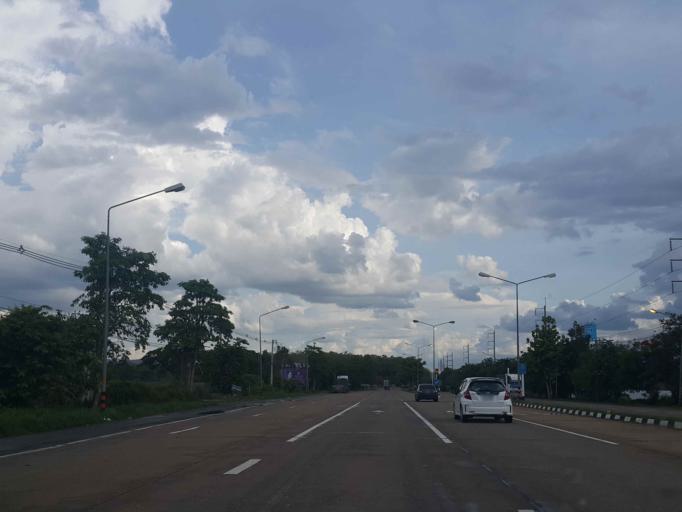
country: TH
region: Phrae
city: Den Chai
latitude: 17.9938
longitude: 100.0989
